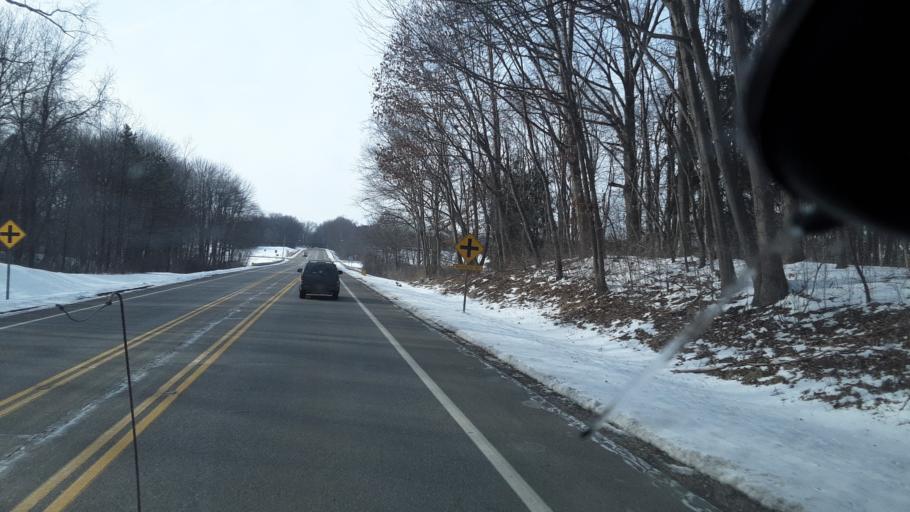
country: US
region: Ohio
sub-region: Stark County
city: Hartville
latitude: 41.0313
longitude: -81.2728
